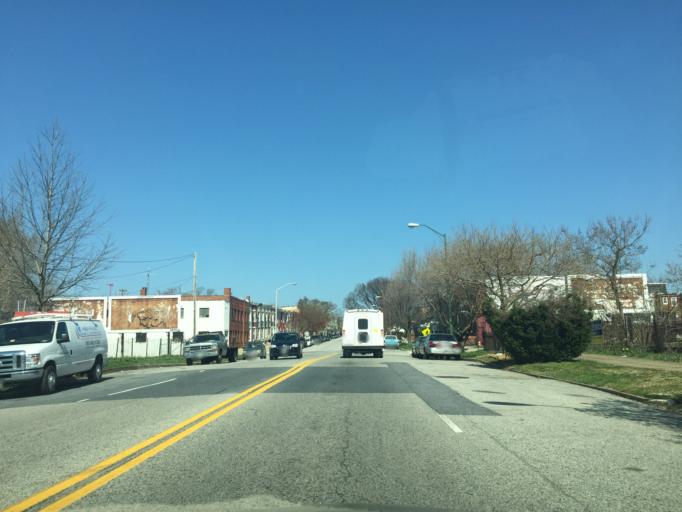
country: US
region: Maryland
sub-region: City of Baltimore
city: Baltimore
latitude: 39.3182
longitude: -76.6208
